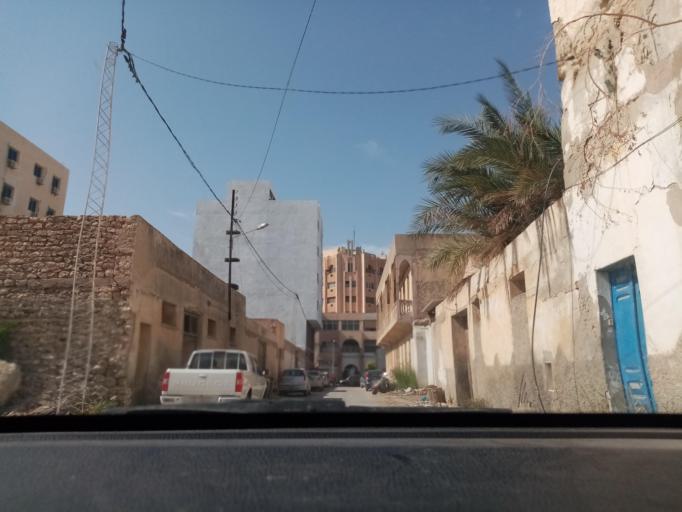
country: TN
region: Qabis
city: Gabes
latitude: 33.8868
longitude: 10.1045
